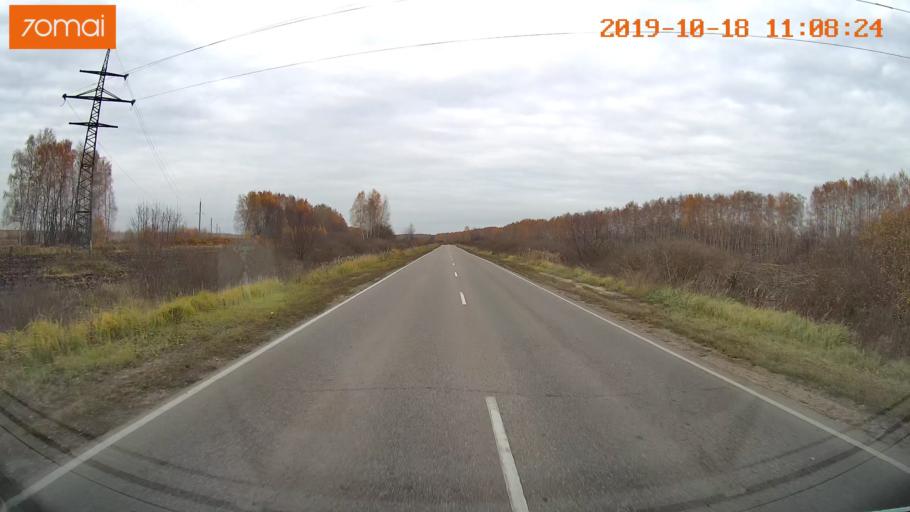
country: RU
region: Tula
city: Kimovsk
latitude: 53.9376
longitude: 38.5374
